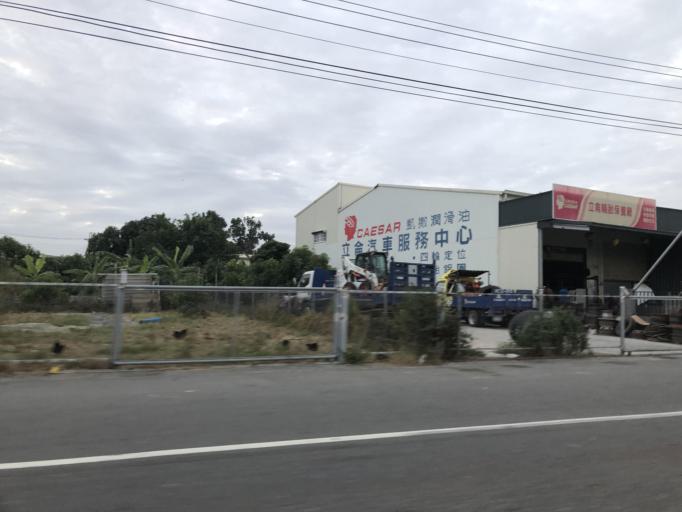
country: TW
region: Taiwan
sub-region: Tainan
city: Tainan
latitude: 23.0231
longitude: 120.2991
